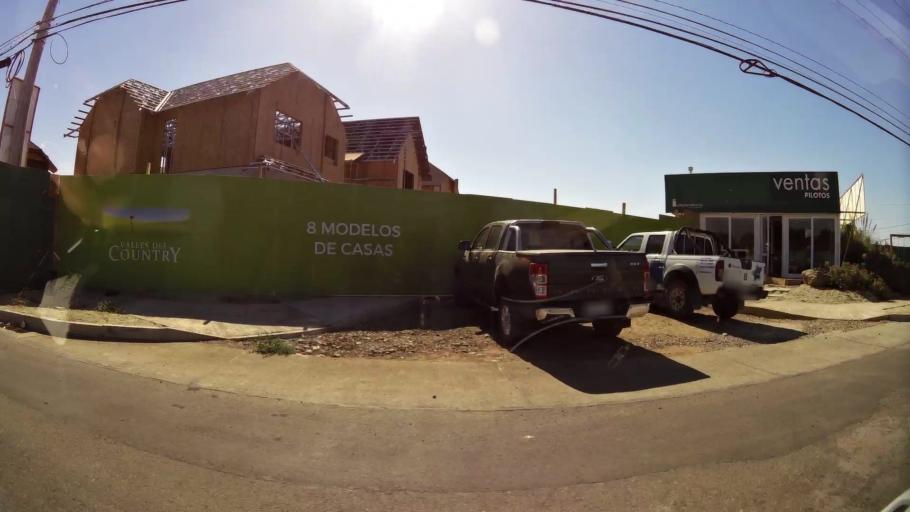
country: CL
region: Maule
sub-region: Provincia de Talca
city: Talca
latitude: -35.4185
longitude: -71.6092
